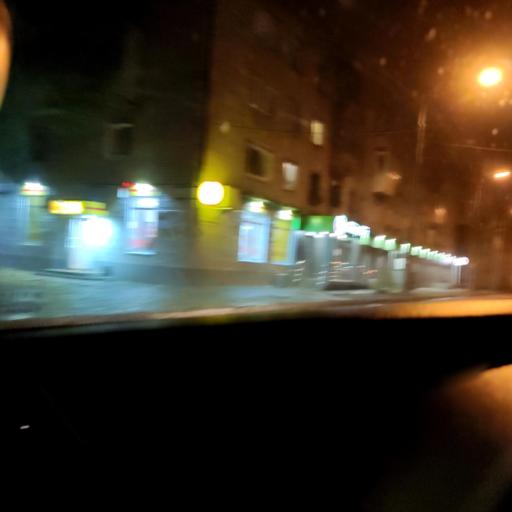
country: RU
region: Samara
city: Petra-Dubrava
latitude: 53.2377
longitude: 50.2887
